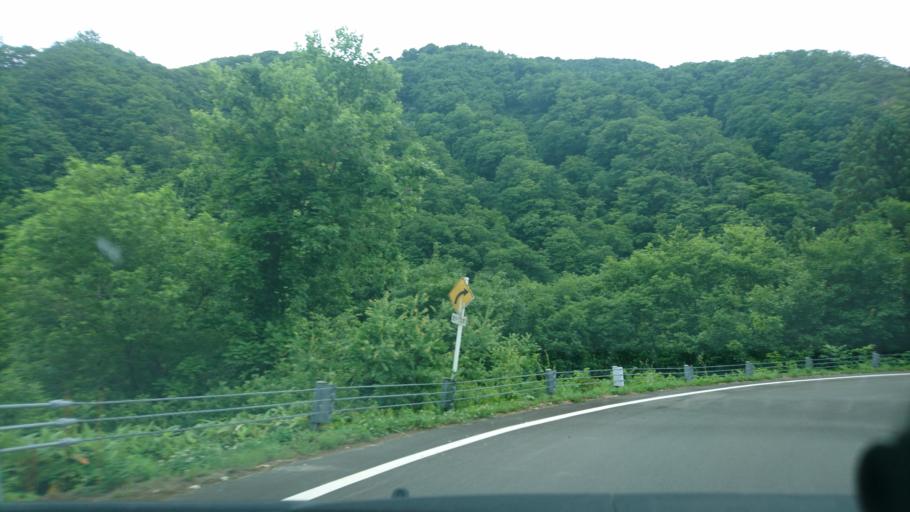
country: JP
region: Akita
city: Yuzawa
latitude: 39.1667
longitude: 140.7428
